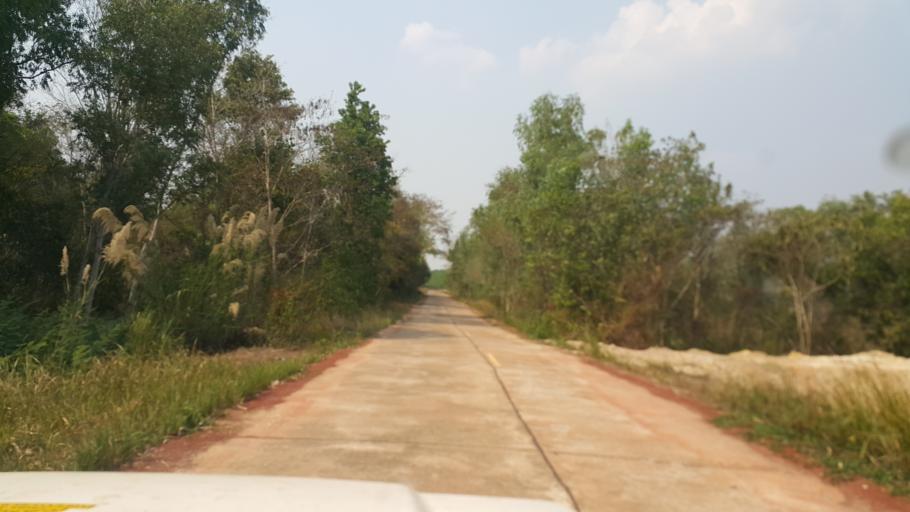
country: TH
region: Nakhon Phanom
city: Ban Phaeng
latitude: 17.9634
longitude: 104.1549
